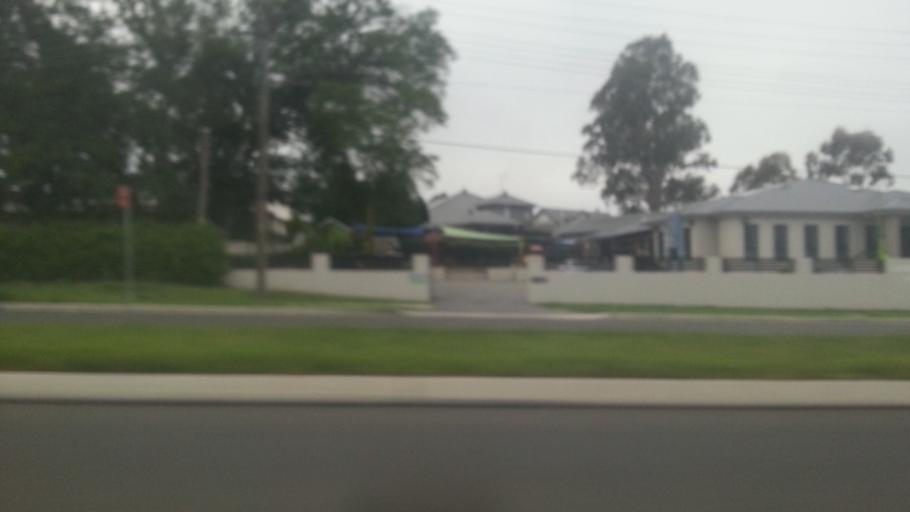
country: AU
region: New South Wales
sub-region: Camden
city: Camden South
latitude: -34.0937
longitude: 150.6946
